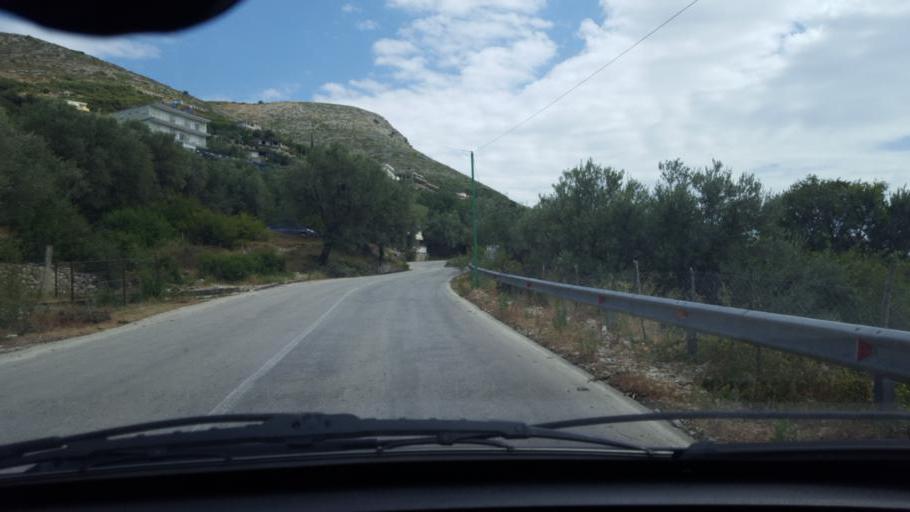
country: AL
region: Vlore
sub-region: Rrethi i Sarandes
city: Lukove
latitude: 40.0646
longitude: 19.8539
